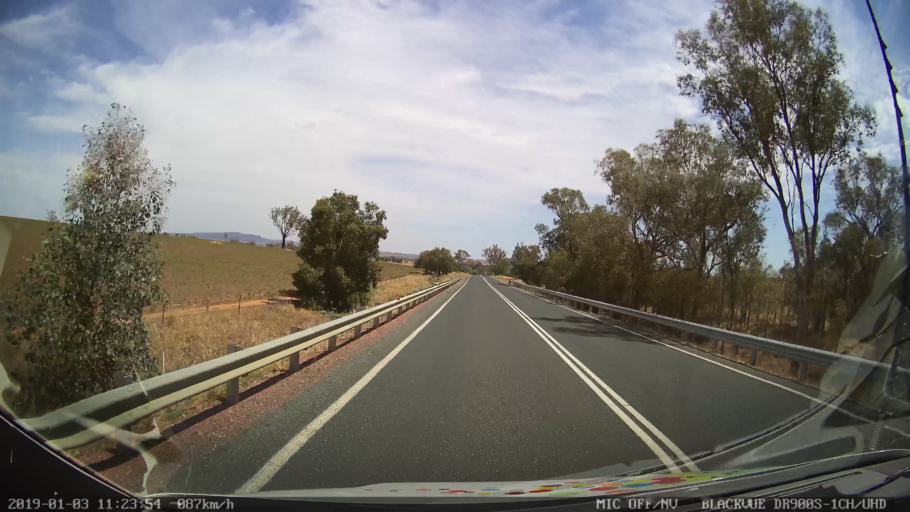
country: AU
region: New South Wales
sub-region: Weddin
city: Grenfell
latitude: -34.0580
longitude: 148.2391
